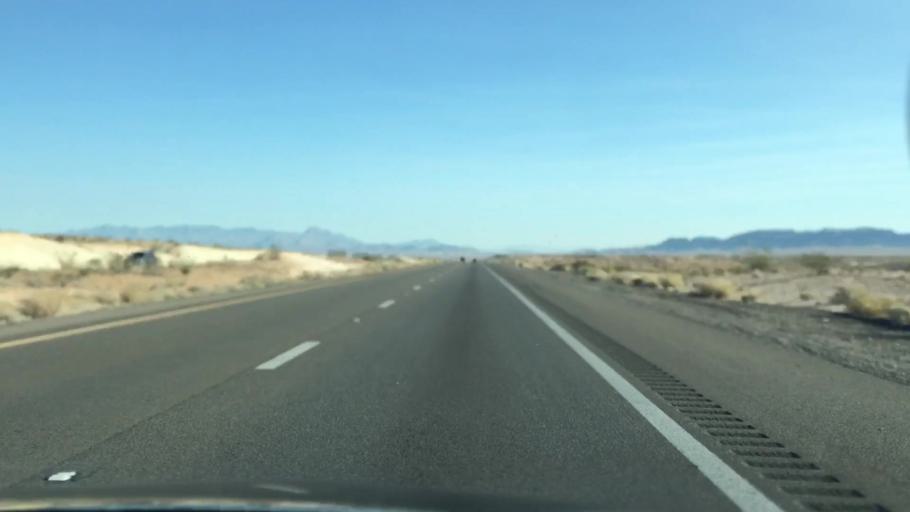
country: US
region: Nevada
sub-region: Clark County
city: Moapa Town
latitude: 36.5208
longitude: -114.7360
